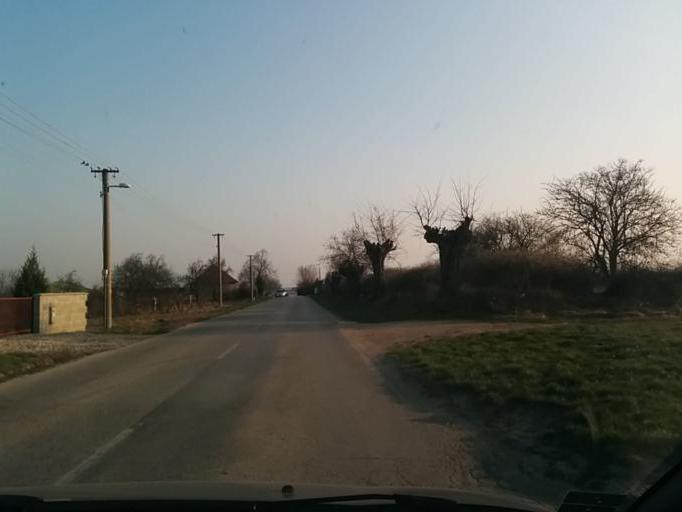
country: SK
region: Trnavsky
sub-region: Okres Galanta
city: Galanta
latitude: 48.2988
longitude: 17.7681
